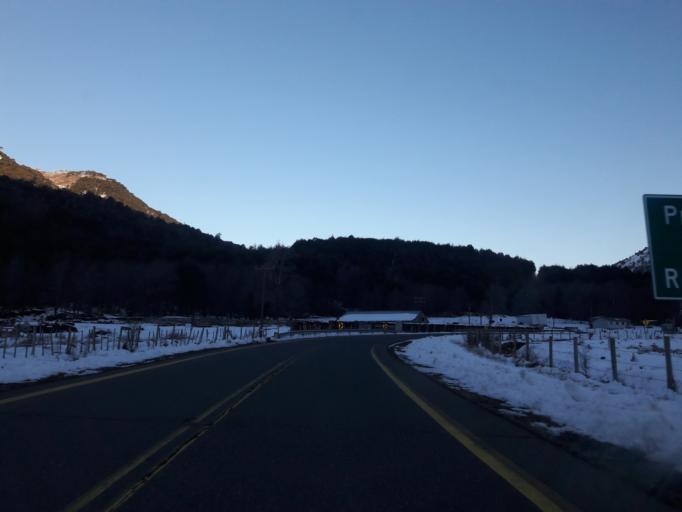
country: CL
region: Araucania
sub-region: Provincia de Cautin
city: Vilcun
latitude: -38.4996
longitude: -71.5198
